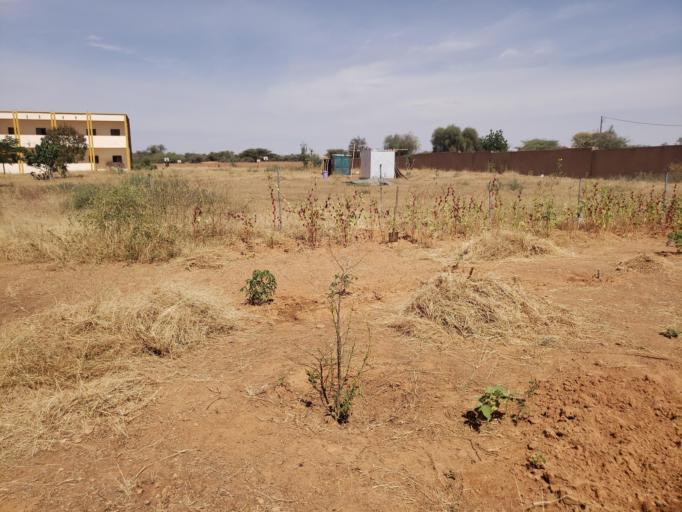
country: SN
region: Louga
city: Ndibene Dahra
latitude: 15.3991
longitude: -15.1321
